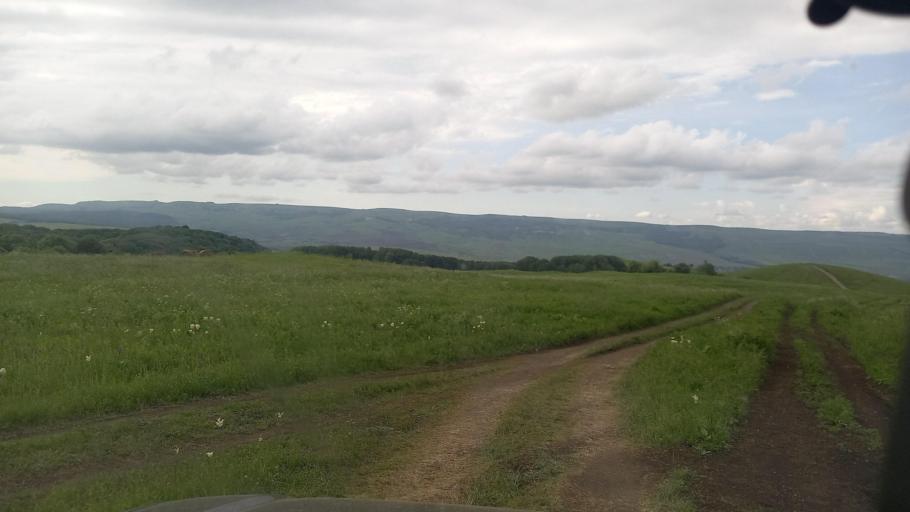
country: RU
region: Krasnodarskiy
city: Peredovaya
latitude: 44.0558
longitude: 41.3626
